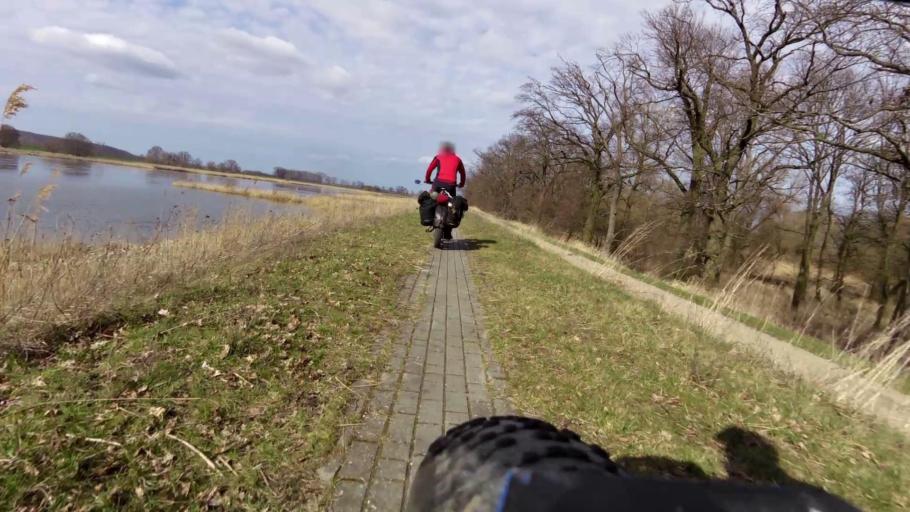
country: DE
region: Brandenburg
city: Reitwein
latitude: 52.4691
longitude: 14.6136
